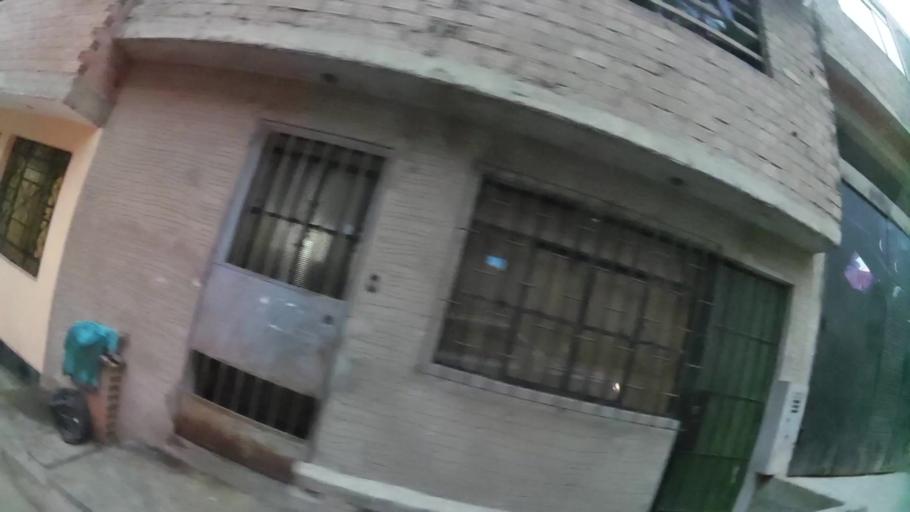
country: PE
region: Lima
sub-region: Lima
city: Surco
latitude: -12.1473
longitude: -76.9771
